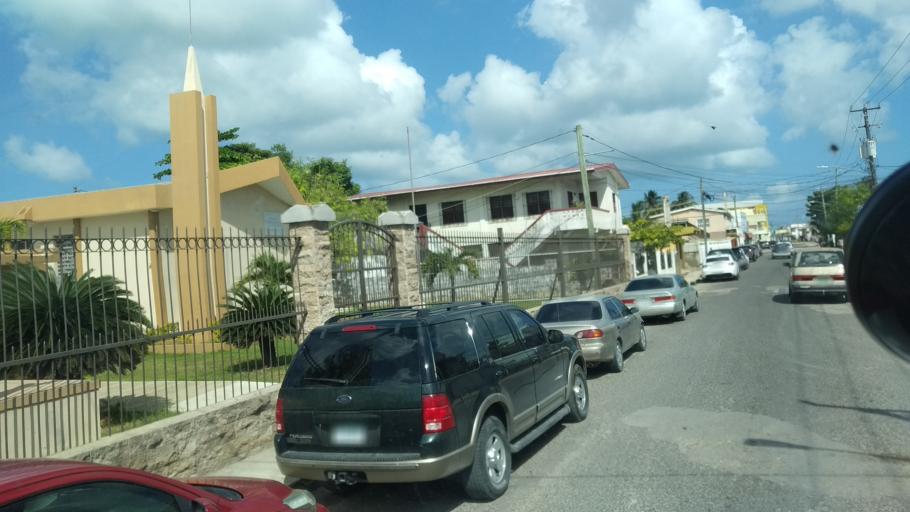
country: BZ
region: Belize
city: Belize City
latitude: 17.4952
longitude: -88.1976
